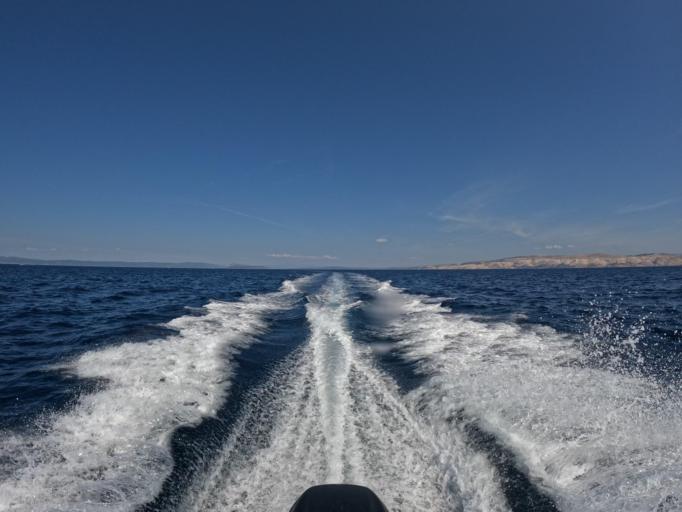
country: HR
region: Primorsko-Goranska
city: Lopar
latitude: 44.8762
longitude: 14.6618
